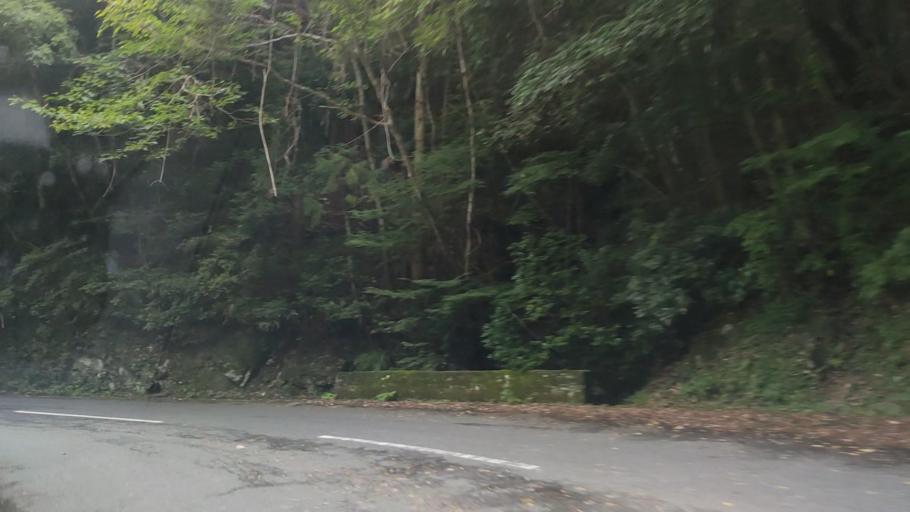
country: JP
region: Wakayama
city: Koya
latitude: 34.2452
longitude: 135.5457
